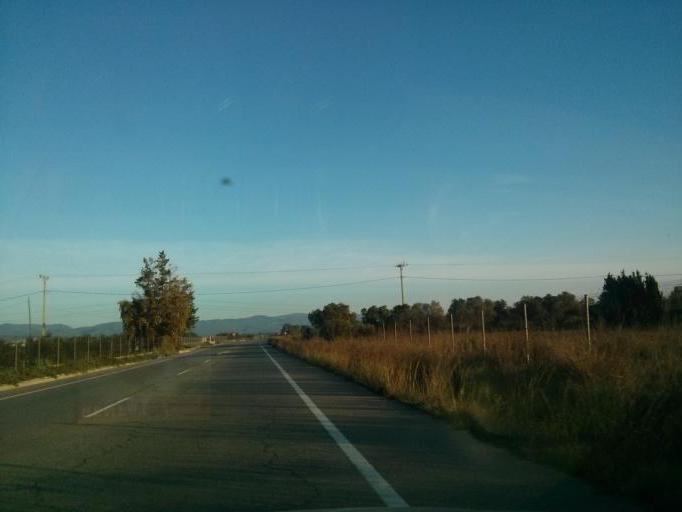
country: ES
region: Catalonia
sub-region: Provincia de Tarragona
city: Santa Oliva
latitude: 41.2438
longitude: 1.5455
